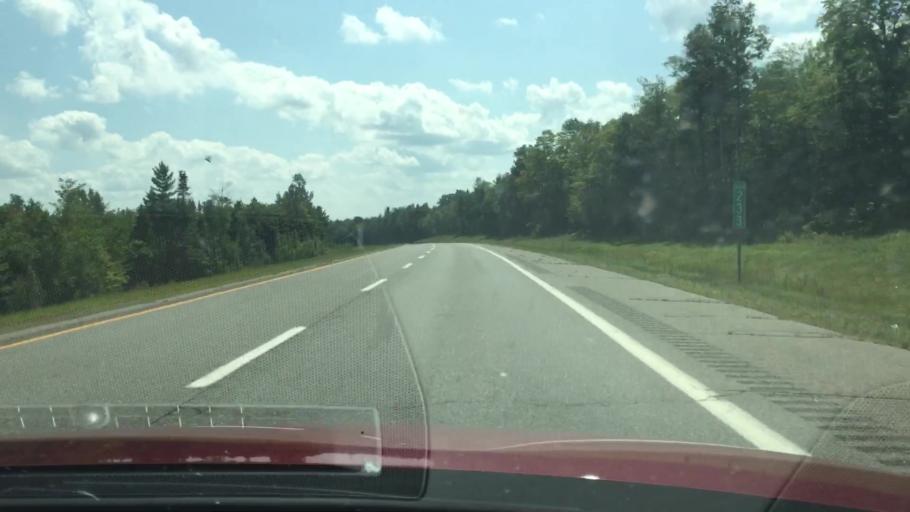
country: US
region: Maine
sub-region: Penobscot County
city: Lincoln
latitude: 45.4551
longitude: -68.5914
